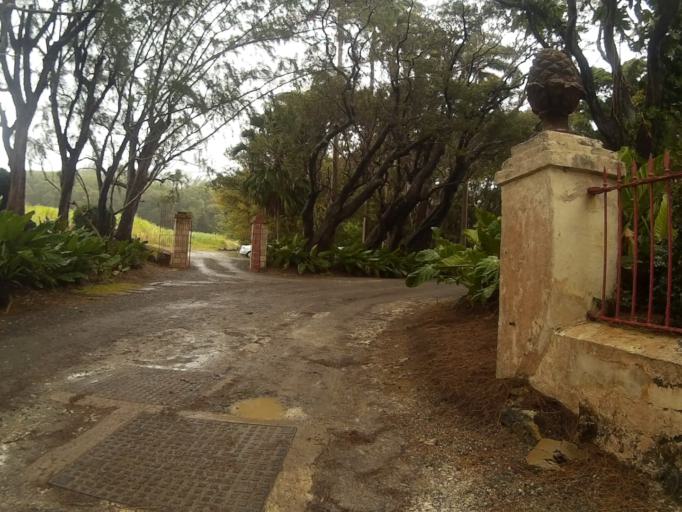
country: BB
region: Saint Andrew
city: Greenland
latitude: 13.2772
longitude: -59.5887
